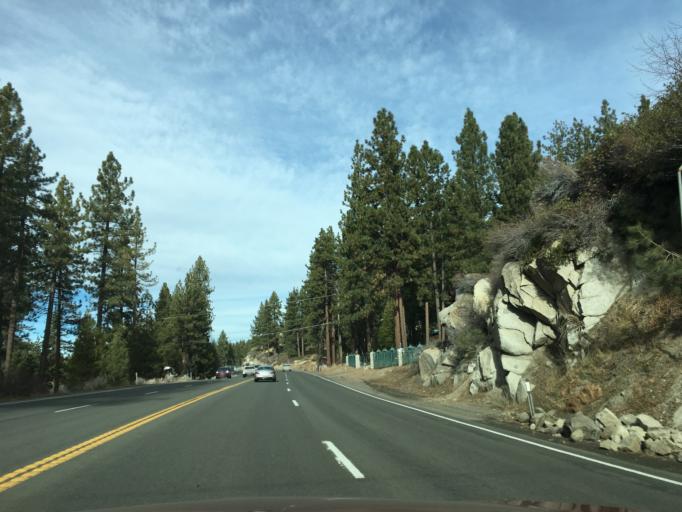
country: US
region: Nevada
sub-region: Douglas County
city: Kingsbury
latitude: 39.0286
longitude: -119.9462
